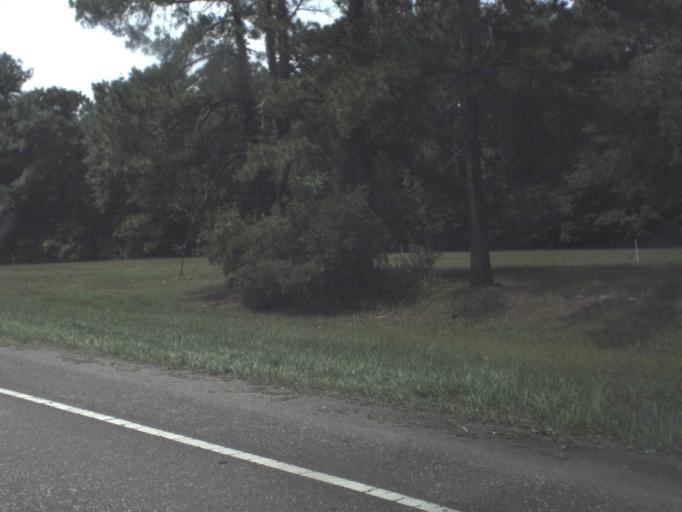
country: US
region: Florida
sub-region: Nassau County
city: Nassau Village-Ratliff
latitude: 30.4110
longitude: -81.7469
